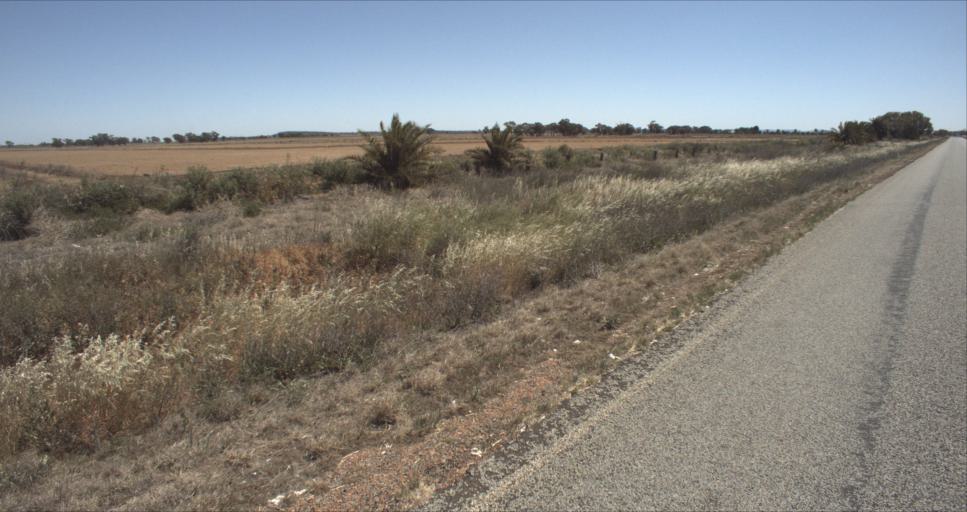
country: AU
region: New South Wales
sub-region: Leeton
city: Leeton
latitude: -34.4513
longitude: 146.2959
